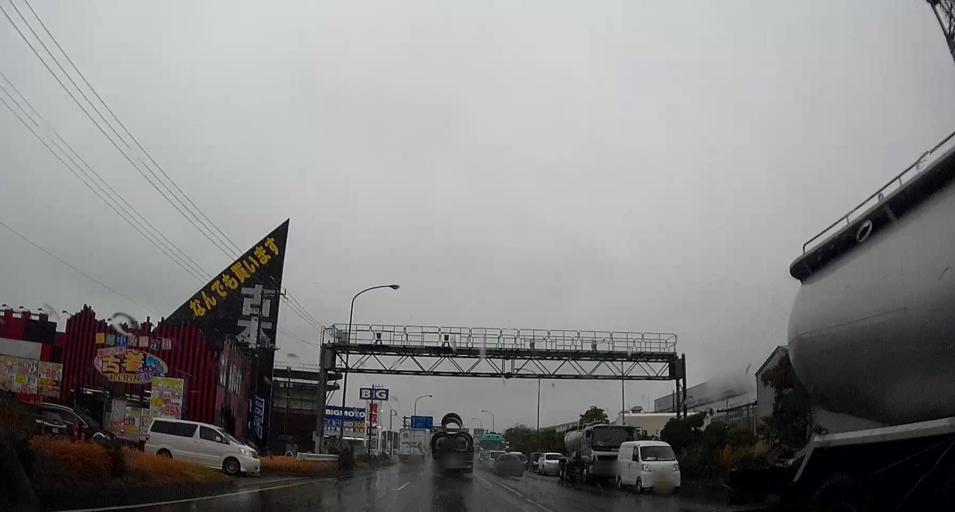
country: JP
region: Chiba
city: Chiba
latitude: 35.5616
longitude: 140.1280
